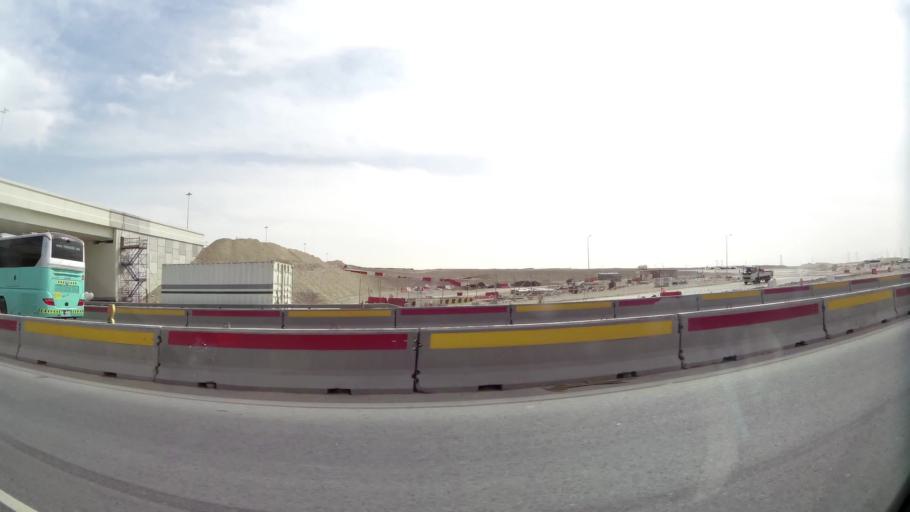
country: QA
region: Baladiyat ar Rayyan
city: Ar Rayyan
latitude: 25.3316
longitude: 51.3315
